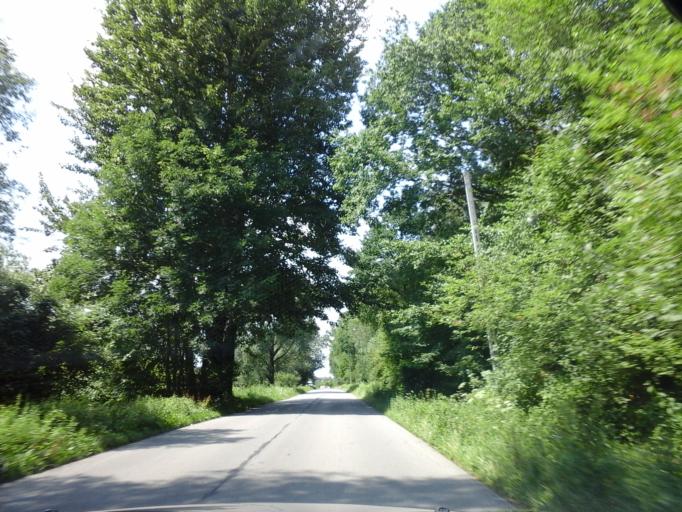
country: PL
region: Lesser Poland Voivodeship
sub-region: Powiat wadowicki
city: Wozniki
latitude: 49.9302
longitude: 19.4910
